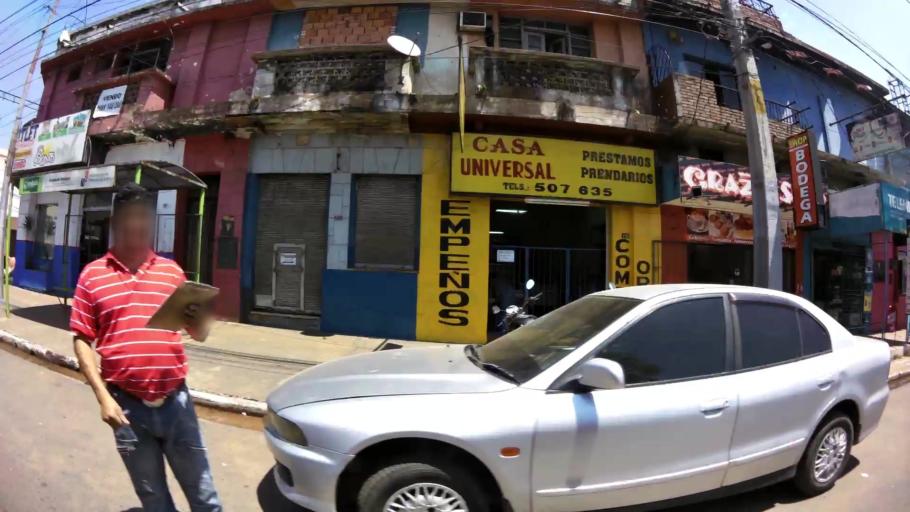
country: PY
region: Central
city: Fernando de la Mora
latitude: -25.3213
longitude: -57.5584
